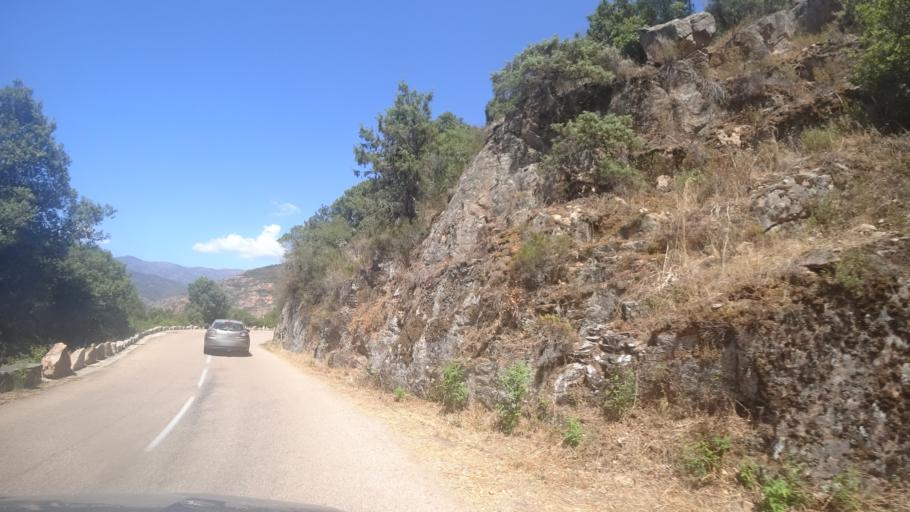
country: FR
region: Corsica
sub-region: Departement de la Corse-du-Sud
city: Cargese
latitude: 42.2601
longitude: 8.6891
